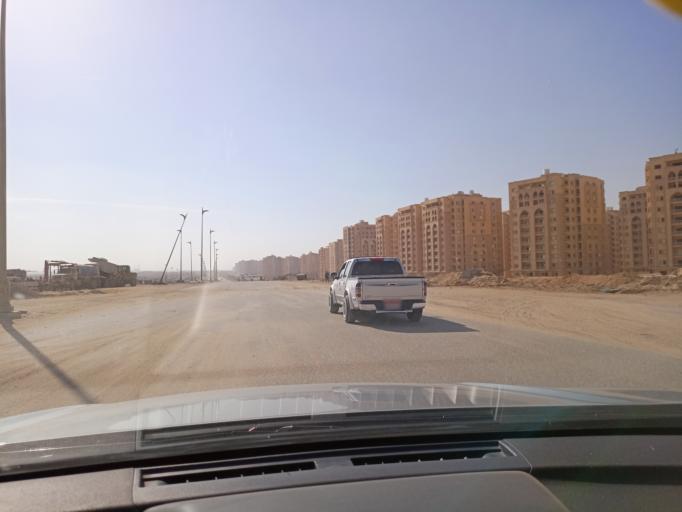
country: EG
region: Muhafazat al Qalyubiyah
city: Al Khankah
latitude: 30.0241
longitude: 31.6743
